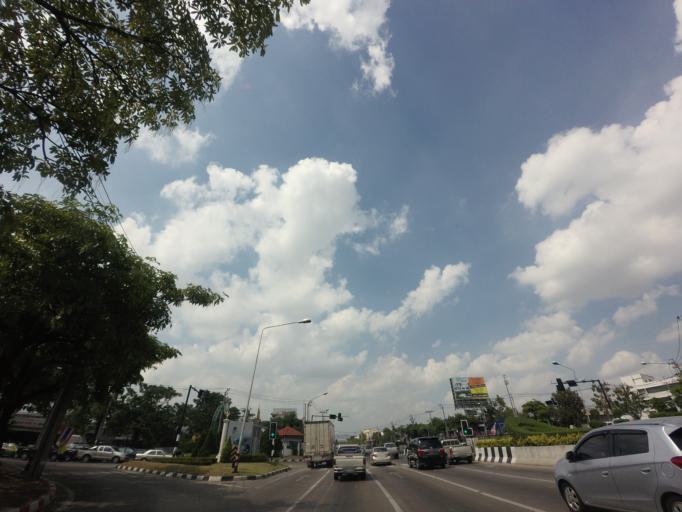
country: TH
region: Bangkok
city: Lat Phrao
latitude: 13.8292
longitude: 100.6236
